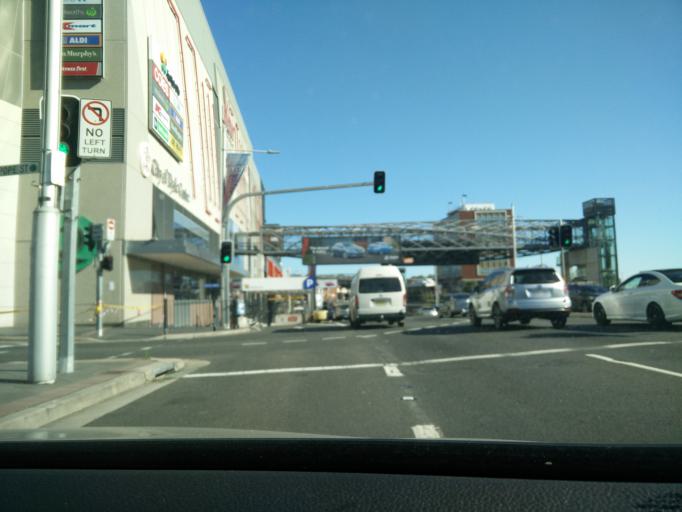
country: AU
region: New South Wales
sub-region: Ryde
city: Denistone
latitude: -33.8106
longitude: 151.1059
